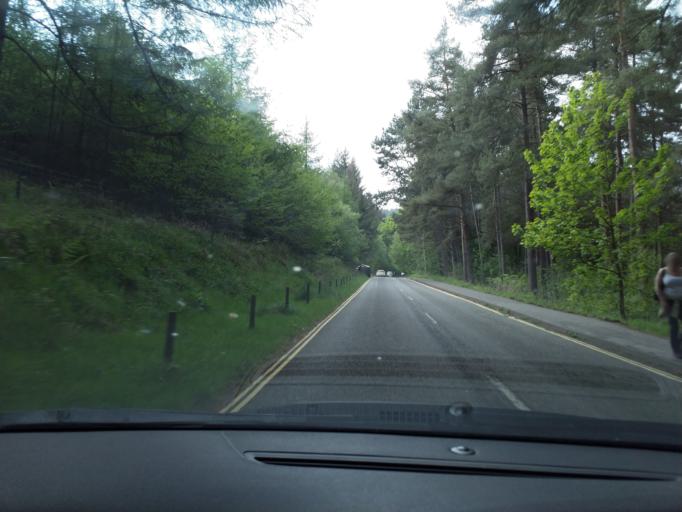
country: GB
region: England
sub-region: Derbyshire
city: Hope Valley
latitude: 53.3955
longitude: -1.7384
